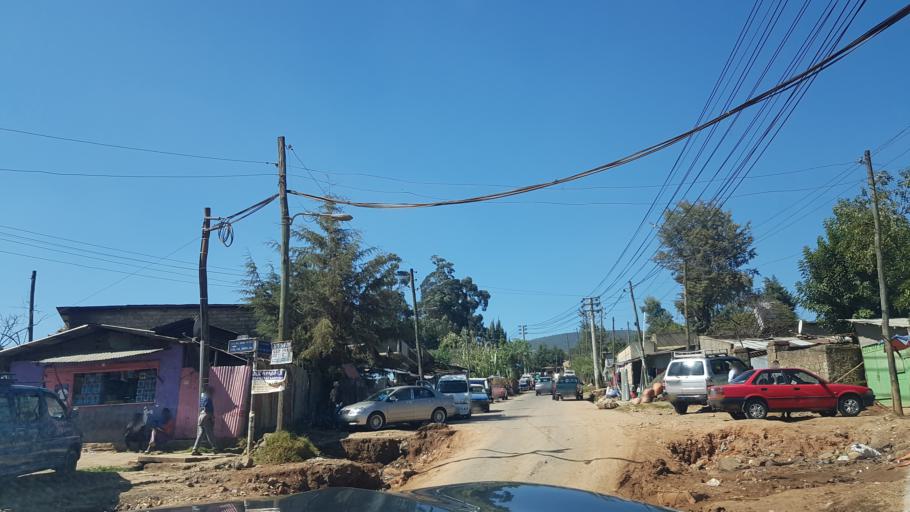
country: ET
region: Adis Abeba
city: Addis Ababa
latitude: 9.0526
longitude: 38.7498
